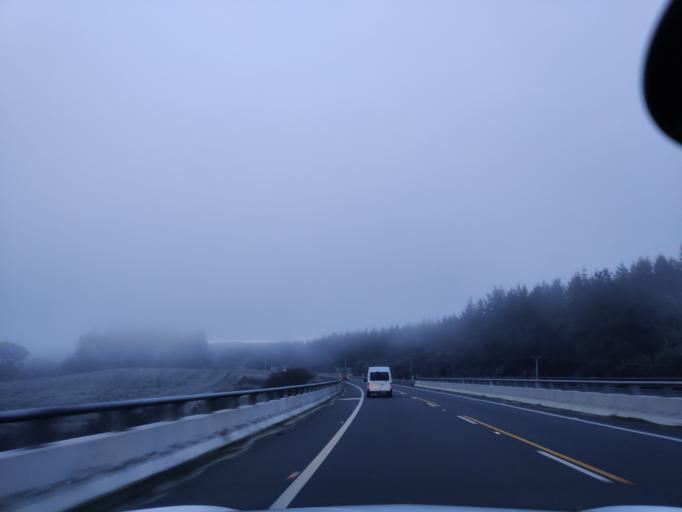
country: NZ
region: Waikato
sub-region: South Waikato District
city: Tokoroa
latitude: -38.3924
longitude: 176.0133
